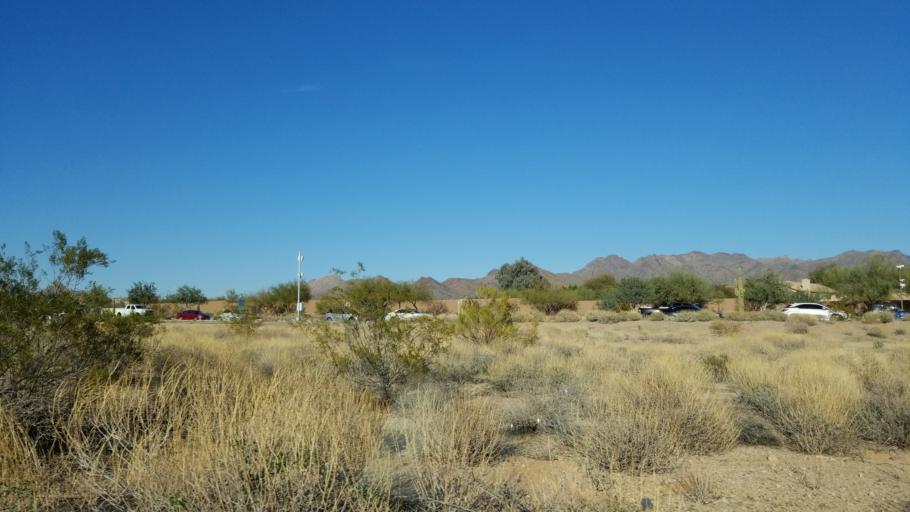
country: US
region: Arizona
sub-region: Maricopa County
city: Paradise Valley
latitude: 33.6600
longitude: -111.8909
